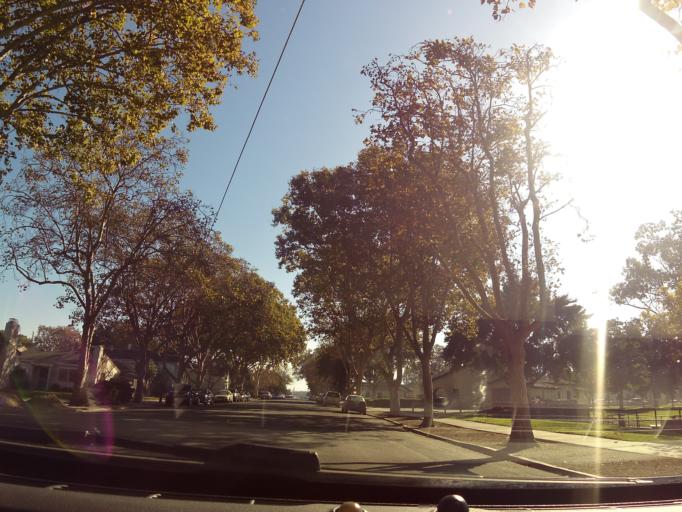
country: US
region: California
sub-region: San Benito County
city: Hollister
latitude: 36.8505
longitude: -121.4070
